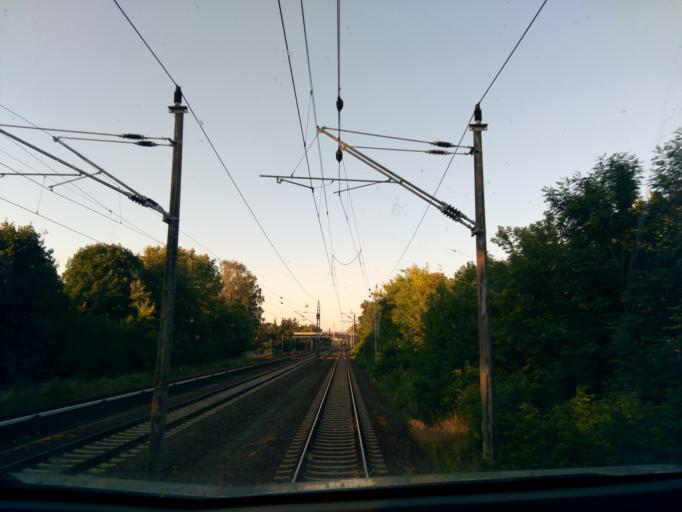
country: DE
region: Brandenburg
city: Konigs Wusterhausen
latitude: 52.3059
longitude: 13.6313
